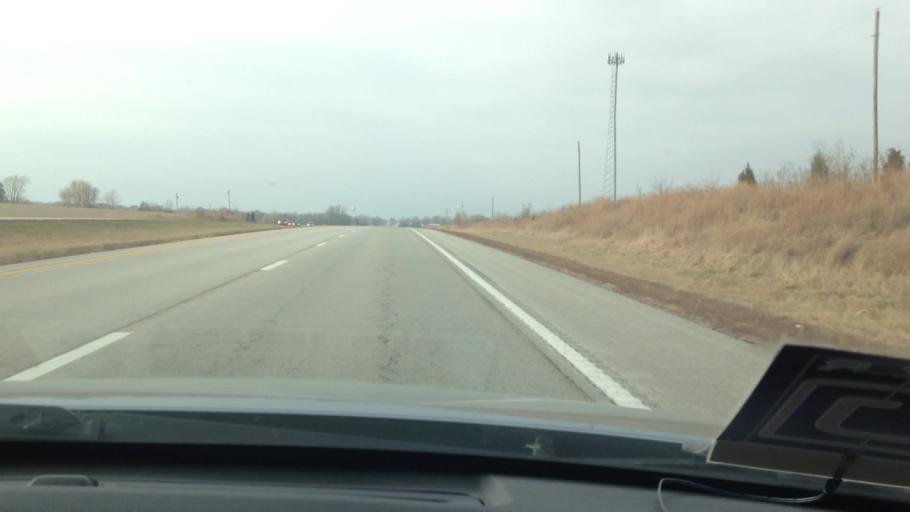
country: US
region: Missouri
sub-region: Cass County
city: Garden City
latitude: 38.5491
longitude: -94.1723
